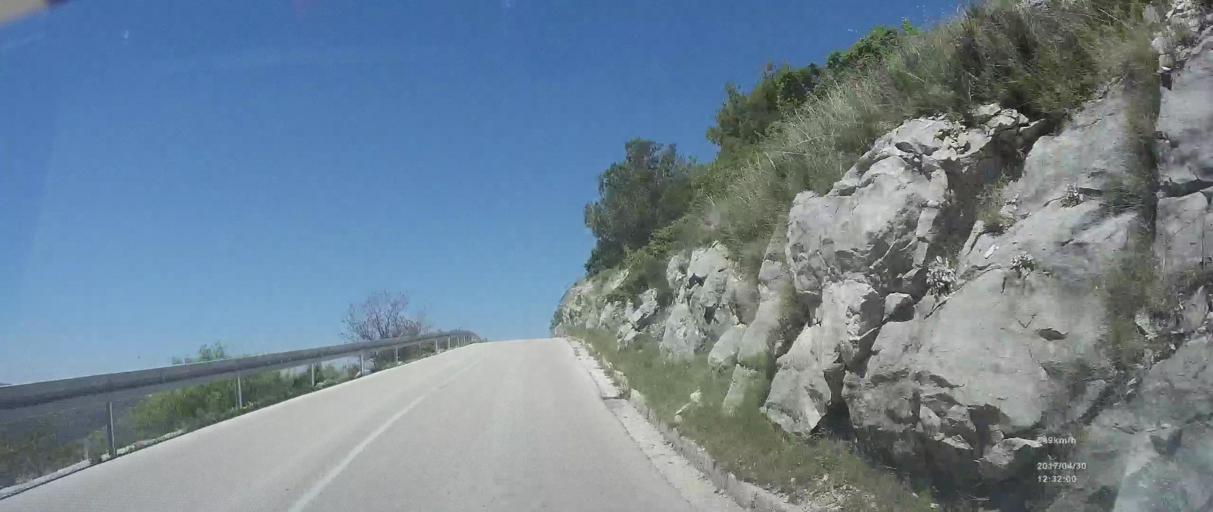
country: HR
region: Splitsko-Dalmatinska
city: Srinjine
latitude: 43.5010
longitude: 16.6072
